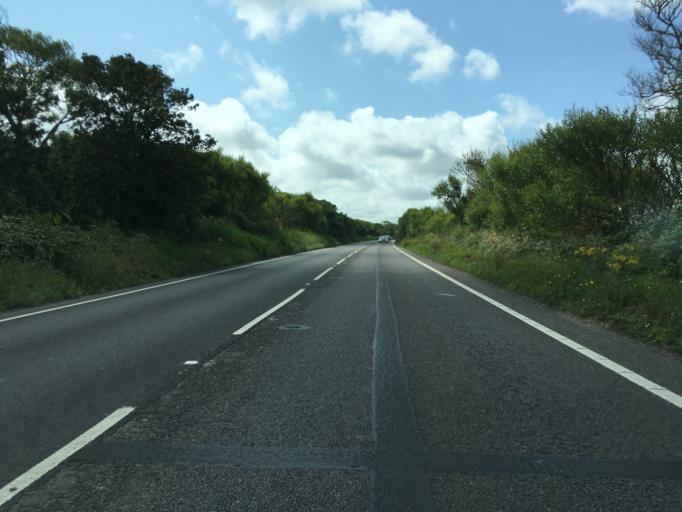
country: GB
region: England
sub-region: East Sussex
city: Pevensey
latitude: 50.8329
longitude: 0.3600
